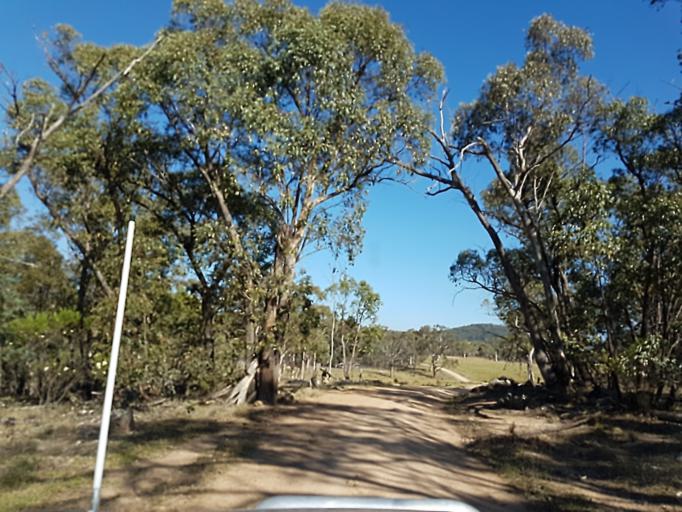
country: AU
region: New South Wales
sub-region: Snowy River
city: Jindabyne
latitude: -37.0377
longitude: 148.2790
